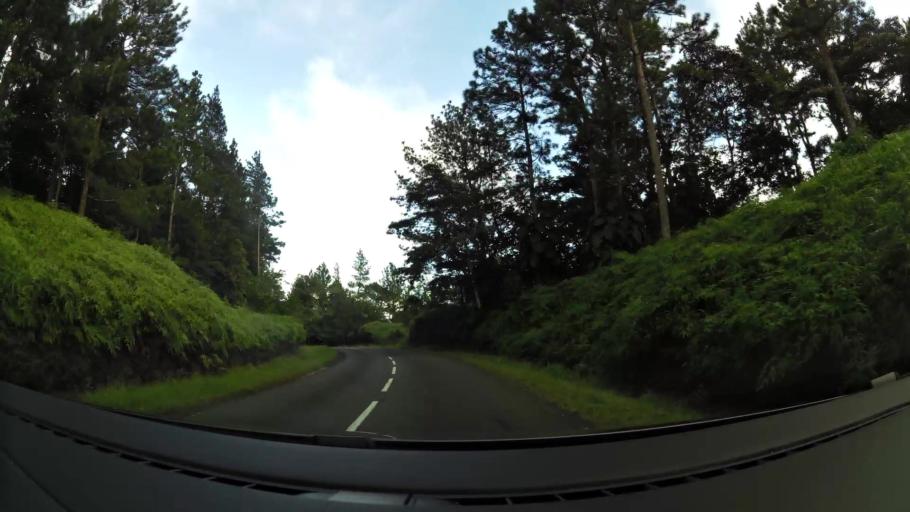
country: GP
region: Guadeloupe
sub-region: Guadeloupe
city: Bouillante
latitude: 16.1778
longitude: -61.7230
